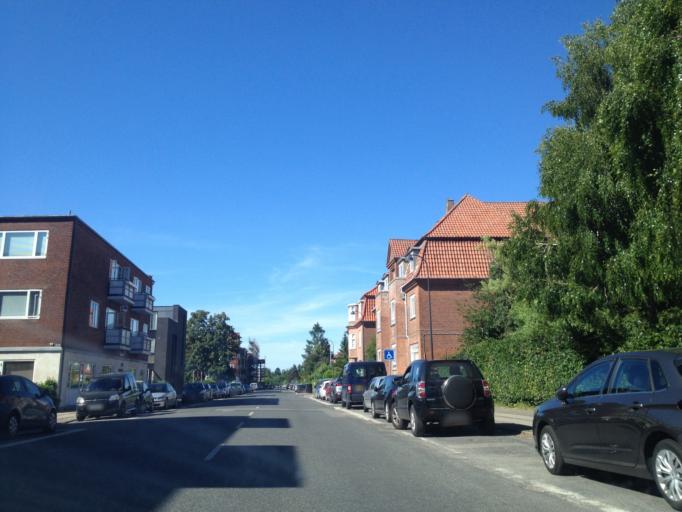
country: DK
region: Capital Region
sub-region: Gentofte Kommune
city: Charlottenlund
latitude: 55.7606
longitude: 12.5856
